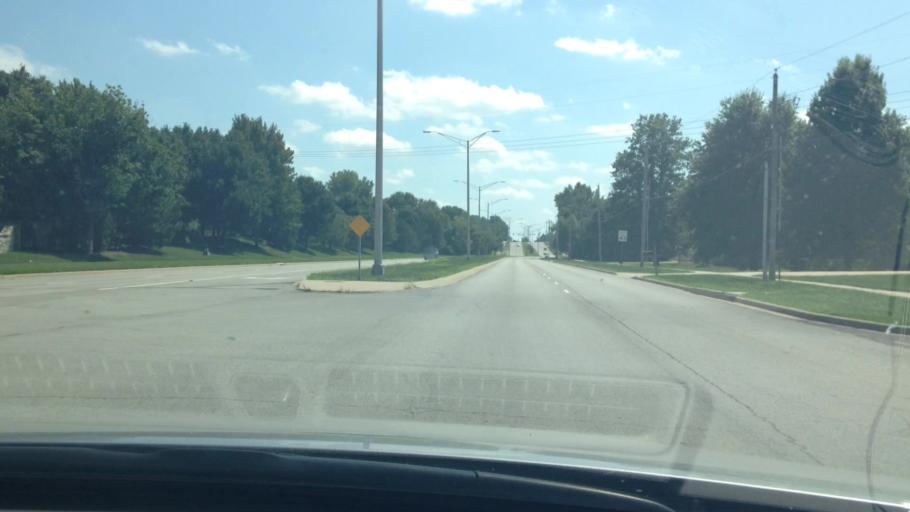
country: US
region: Kansas
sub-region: Johnson County
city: Lenexa
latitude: 38.8612
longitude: -94.7050
